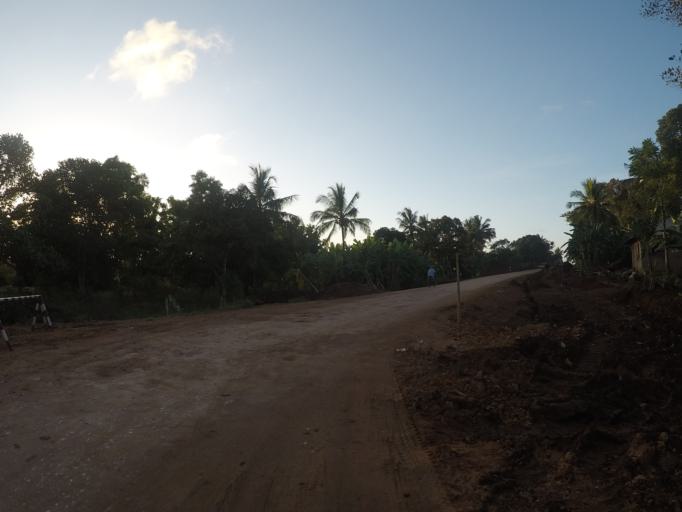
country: TZ
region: Zanzibar North
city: Gamba
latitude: -5.9190
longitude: 39.2996
